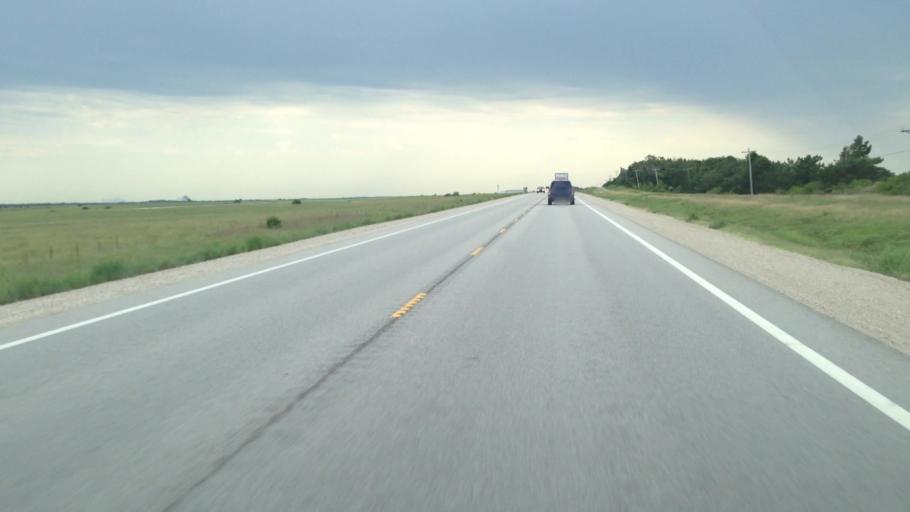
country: US
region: Kansas
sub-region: Coffey County
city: Burlington
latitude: 38.3168
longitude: -95.7290
